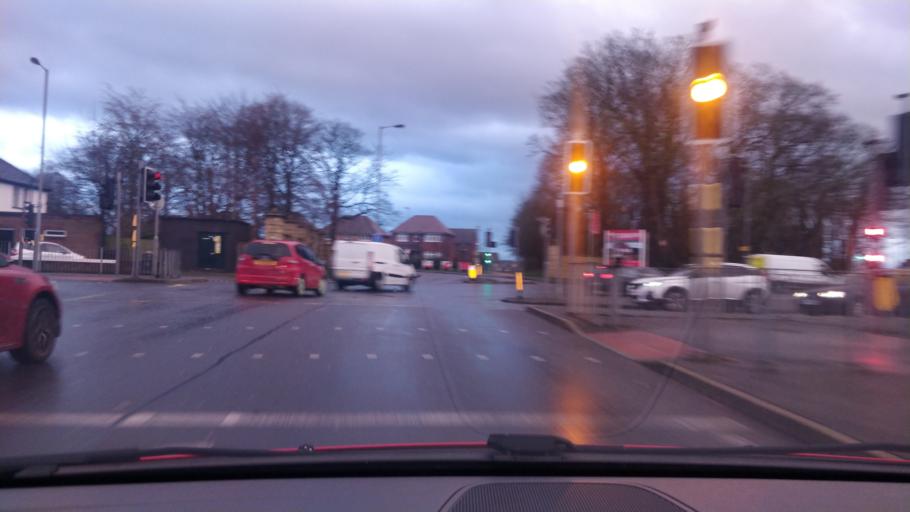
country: GB
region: England
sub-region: Knowsley
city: Huyton
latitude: 53.4112
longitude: -2.8925
